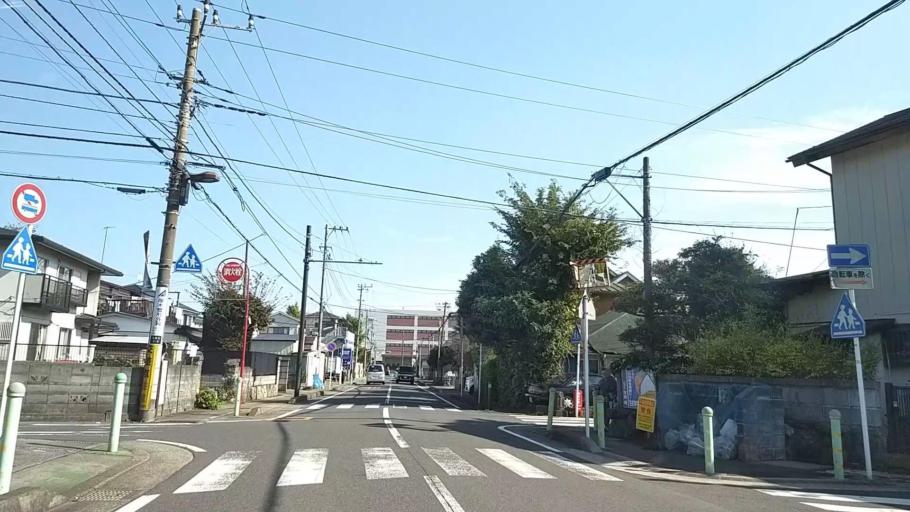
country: JP
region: Kanagawa
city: Atsugi
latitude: 35.4456
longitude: 139.3757
